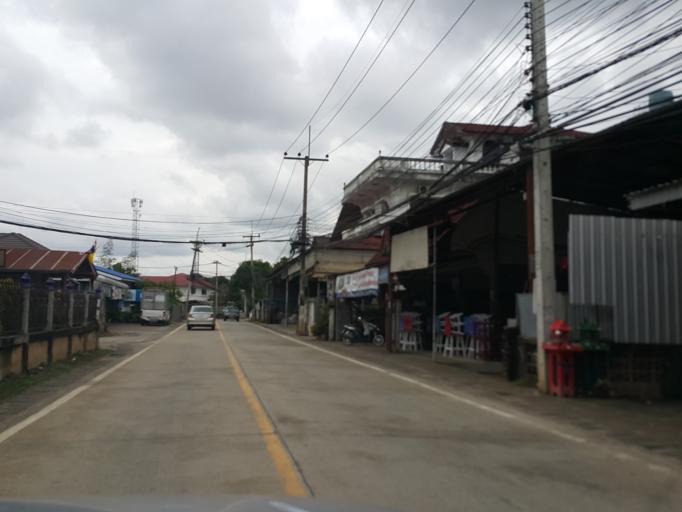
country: TH
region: Lamphun
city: Lamphun
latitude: 18.5770
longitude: 99.0704
